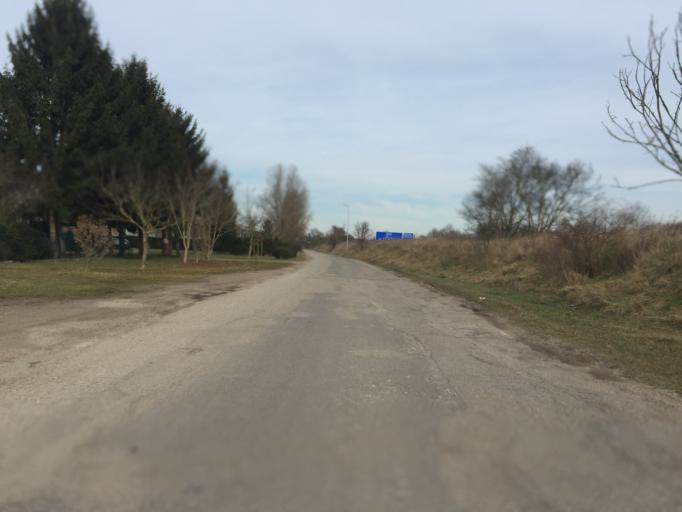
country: DE
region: Hesse
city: Viernheim
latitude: 49.5442
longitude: 8.5585
